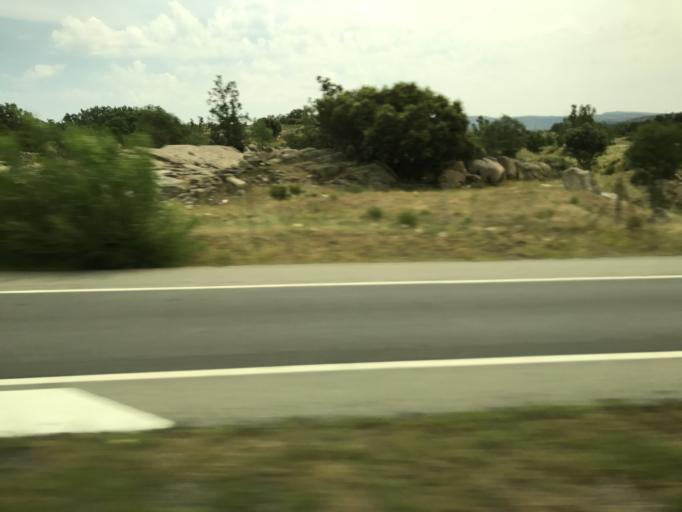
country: ES
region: Madrid
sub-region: Provincia de Madrid
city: La Cabrera
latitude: 40.9093
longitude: -3.6090
